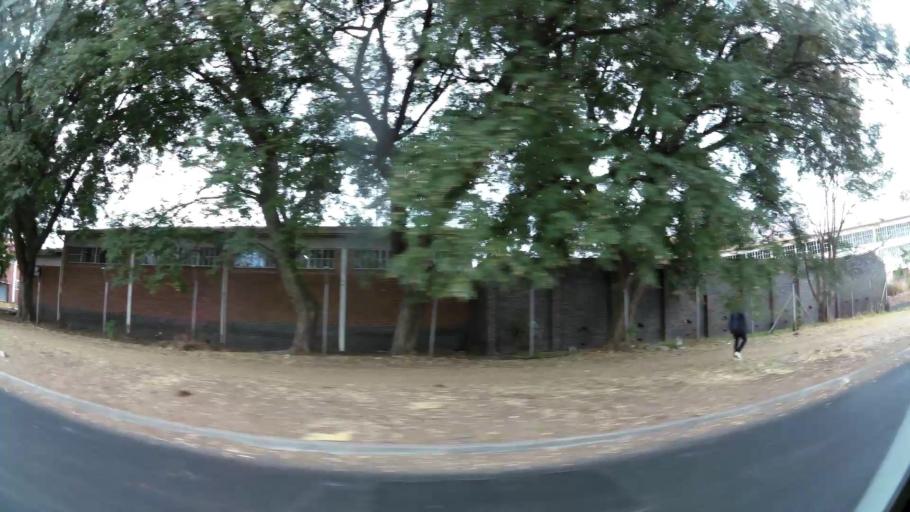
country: ZA
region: Limpopo
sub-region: Capricorn District Municipality
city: Polokwane
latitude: -23.8952
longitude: 29.4509
